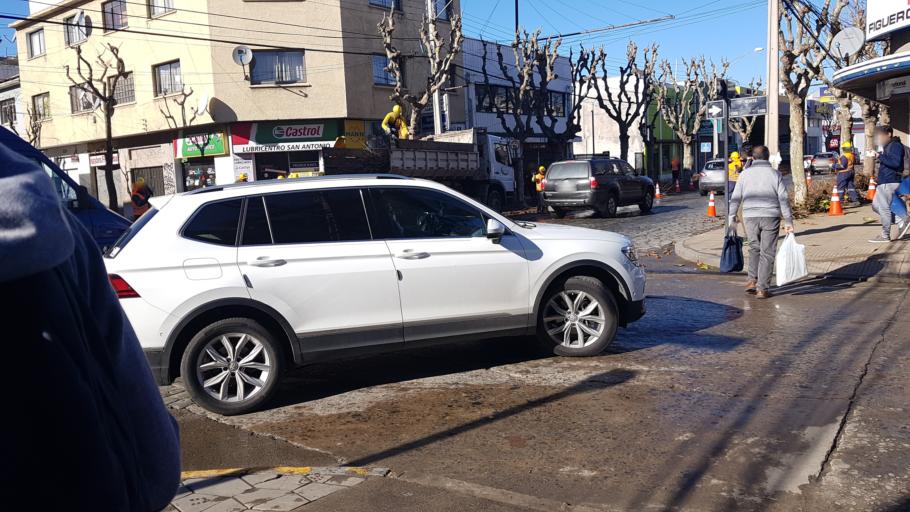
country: CL
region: Valparaiso
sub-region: Provincia de Valparaiso
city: Vina del Mar
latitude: -33.0130
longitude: -71.5433
